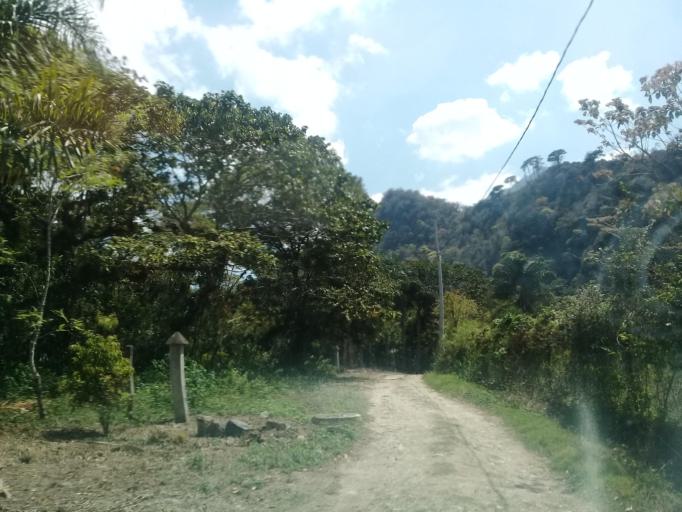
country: MX
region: Veracruz
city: Jalapilla
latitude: 18.8102
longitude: -97.0644
